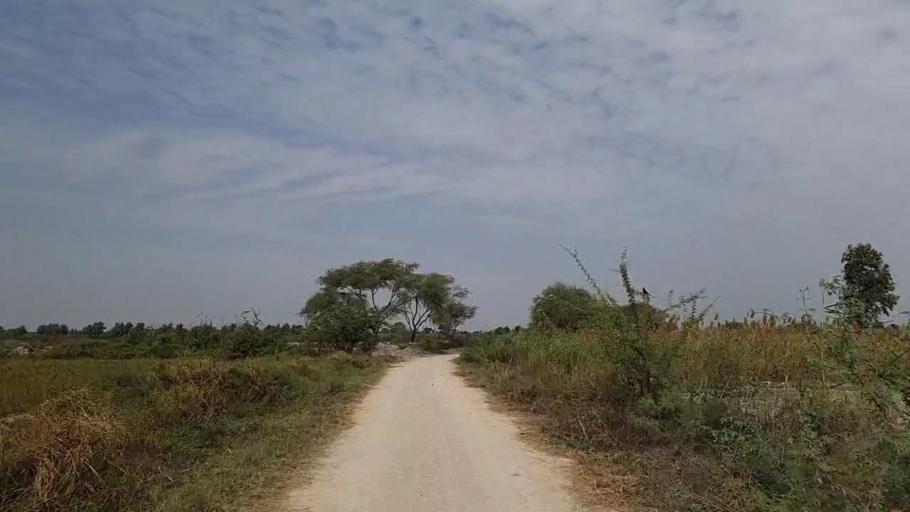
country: PK
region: Sindh
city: Daro Mehar
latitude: 24.7904
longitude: 68.2070
